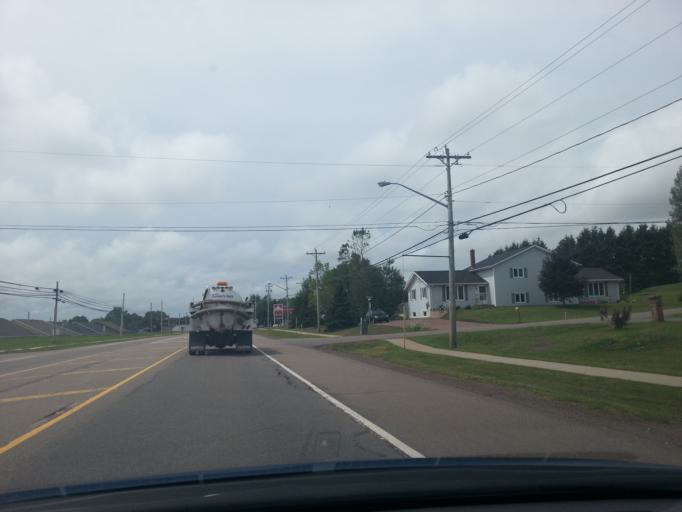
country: CA
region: Prince Edward Island
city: Charlottetown
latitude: 46.2792
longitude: -63.1009
